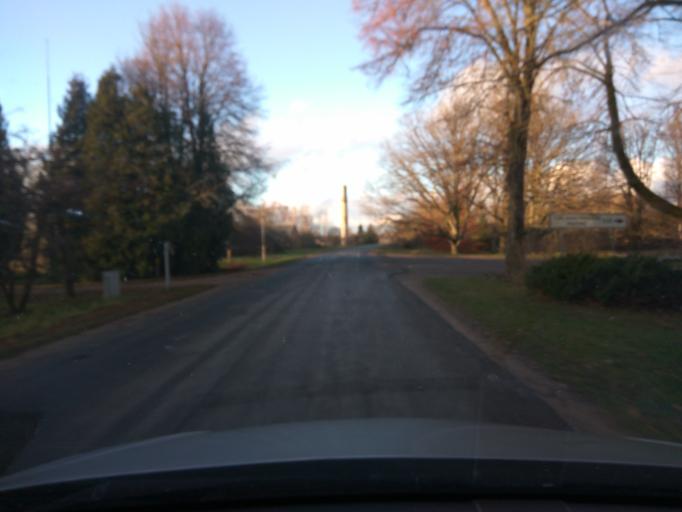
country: LV
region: Aizpute
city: Aizpute
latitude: 56.8316
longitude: 21.7723
